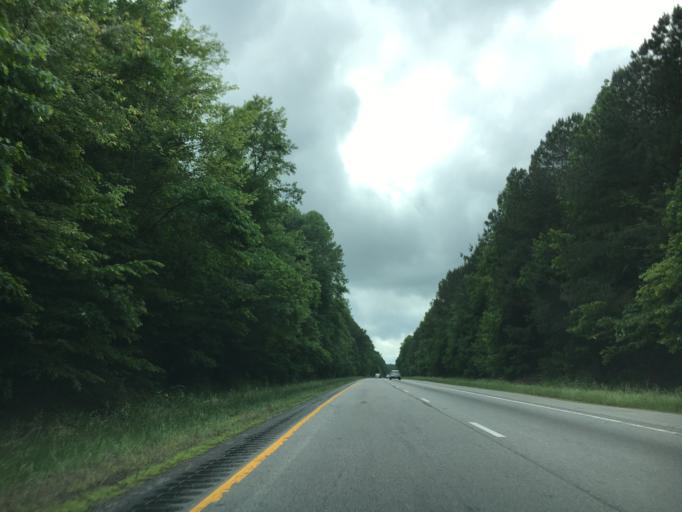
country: US
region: Virginia
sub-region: Mecklenburg County
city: South Hill
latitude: 36.7876
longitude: -78.0066
